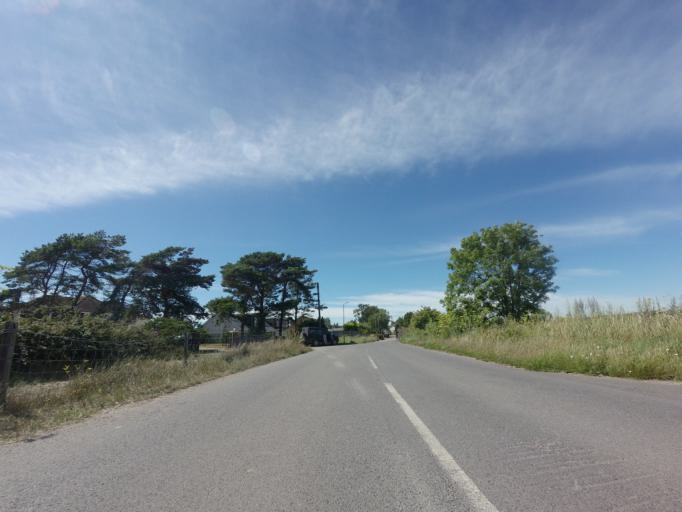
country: GB
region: England
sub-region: Kent
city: Sandwich
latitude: 51.2696
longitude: 1.3632
